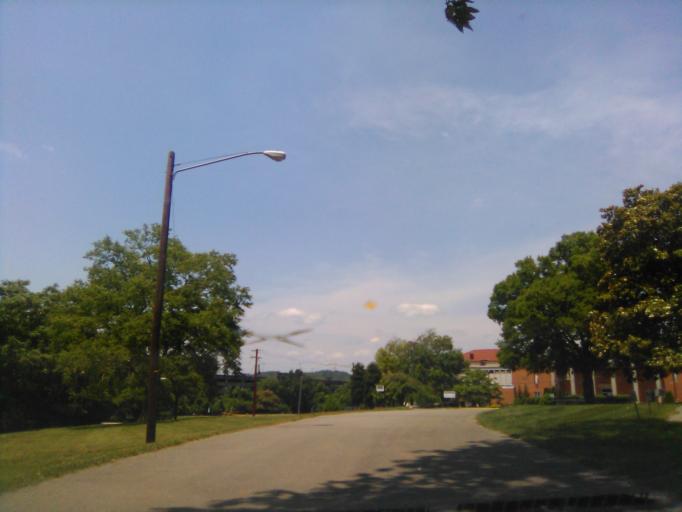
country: US
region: Tennessee
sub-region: Davidson County
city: Belle Meade
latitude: 36.1316
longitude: -86.8431
